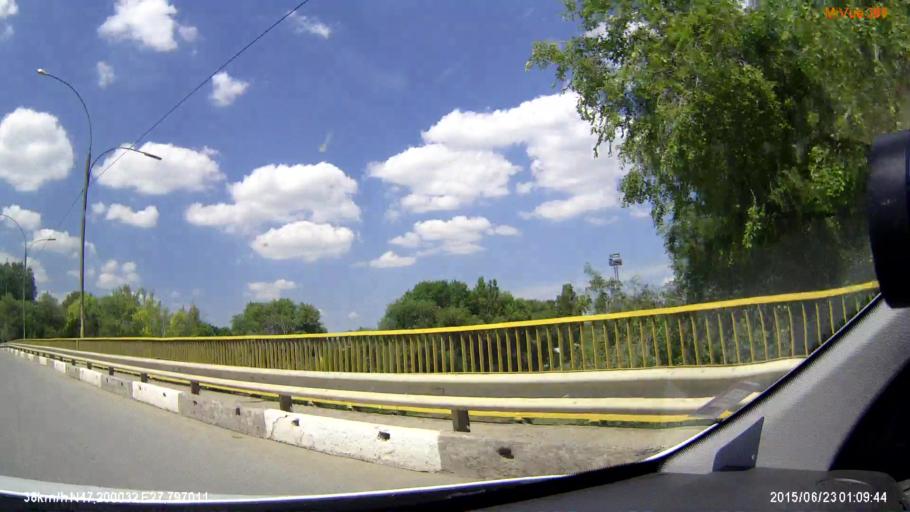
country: MD
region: Ungheni
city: Ungheni
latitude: 47.2000
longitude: 27.7971
